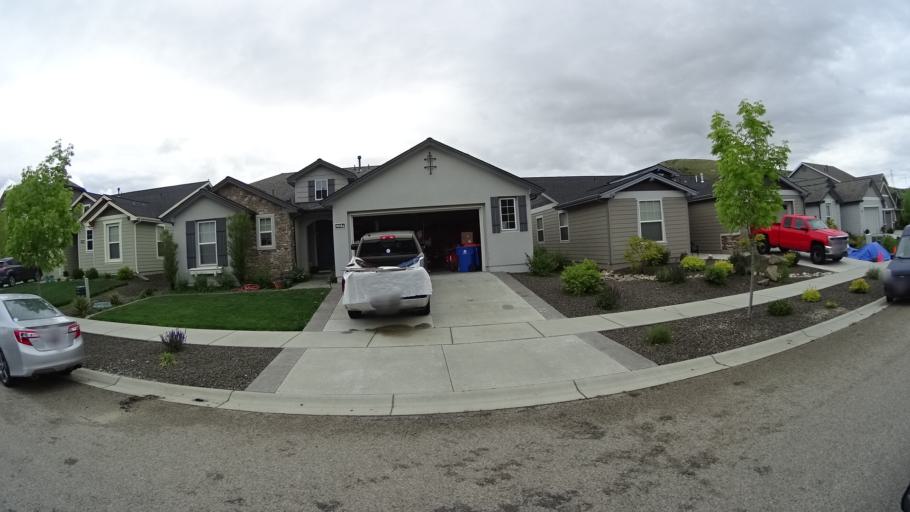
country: US
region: Idaho
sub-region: Ada County
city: Eagle
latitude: 43.7688
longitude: -116.2653
